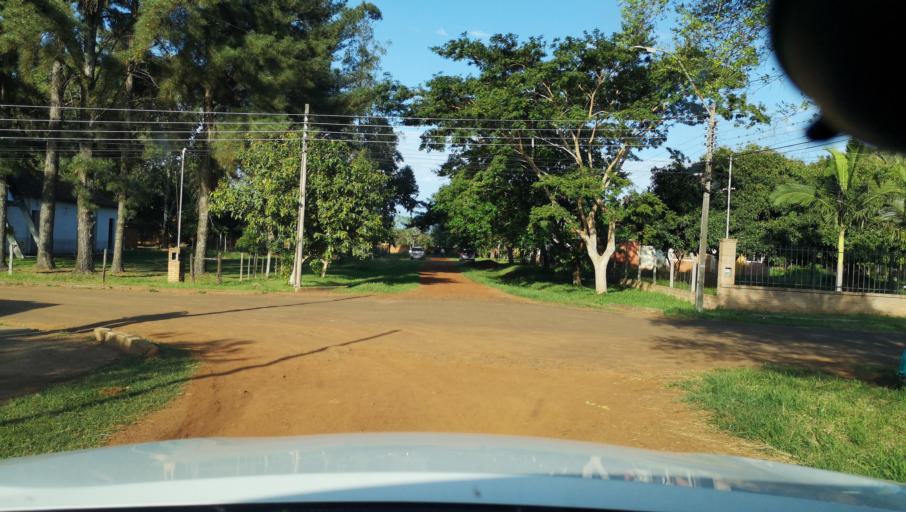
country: PY
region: Itapua
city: Carmen del Parana
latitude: -27.1605
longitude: -56.2450
